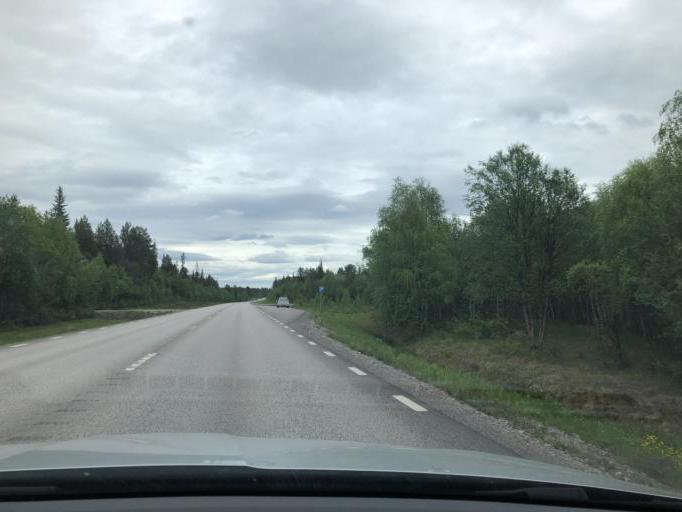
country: SE
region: Norrbotten
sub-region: Gallivare Kommun
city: Malmberget
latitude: 67.6503
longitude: 21.1689
